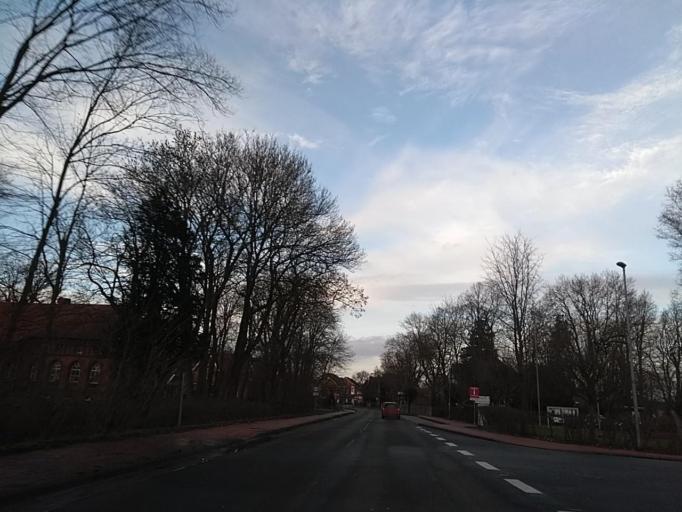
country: DE
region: Lower Saxony
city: Jemgum
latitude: 53.2623
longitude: 7.3838
